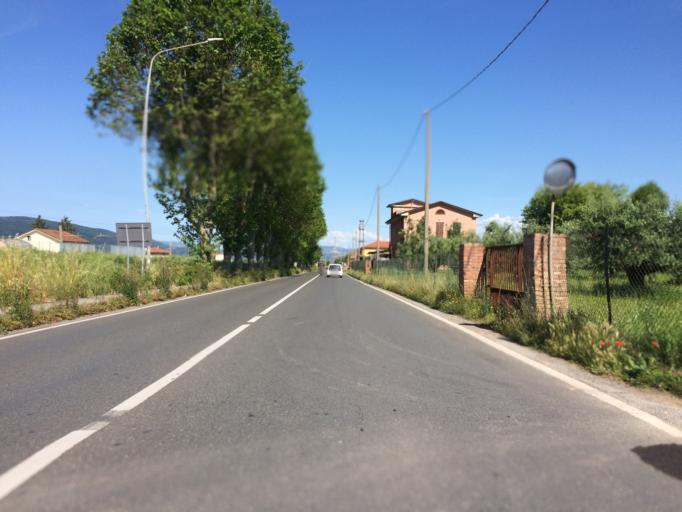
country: IT
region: Liguria
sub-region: Provincia di La Spezia
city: Casano-Dogana-Isola
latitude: 44.0734
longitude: 10.0193
